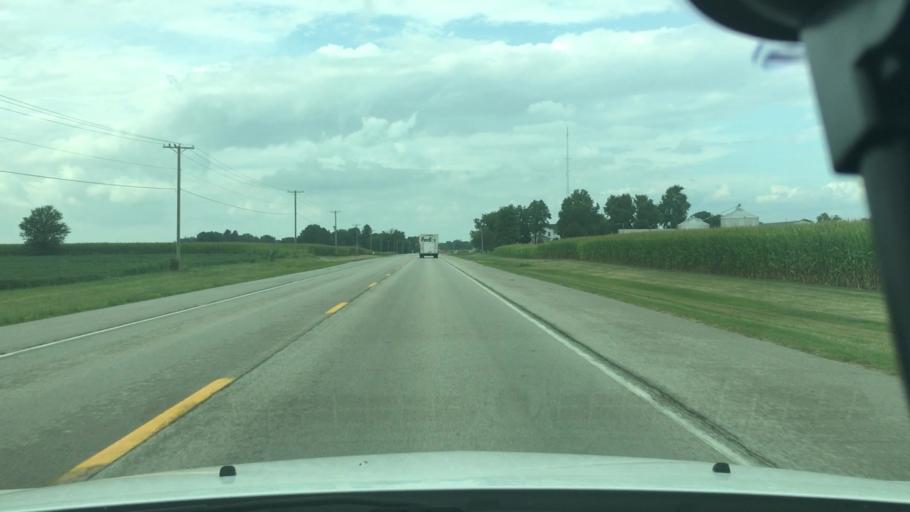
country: US
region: Illinois
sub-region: DeKalb County
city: DeKalb
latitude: 41.8842
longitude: -88.7538
